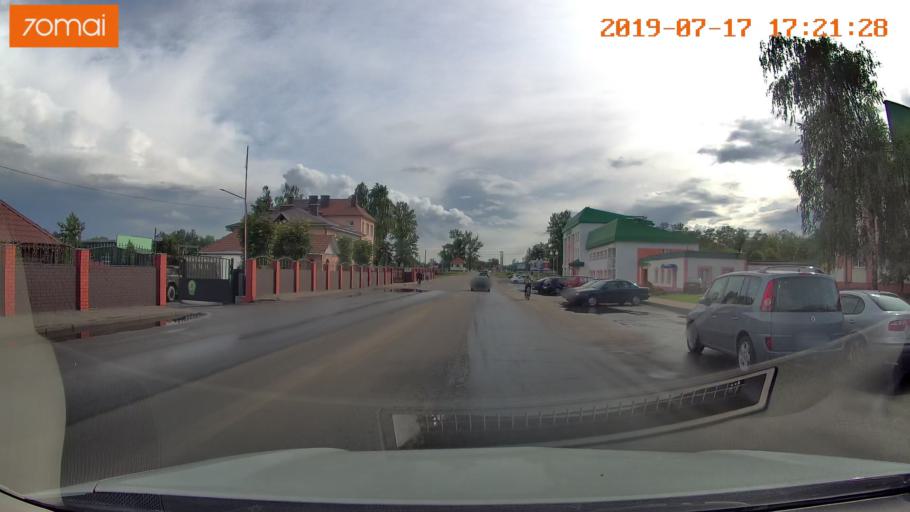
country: BY
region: Mogilev
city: Babruysk
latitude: 53.1477
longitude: 29.1785
